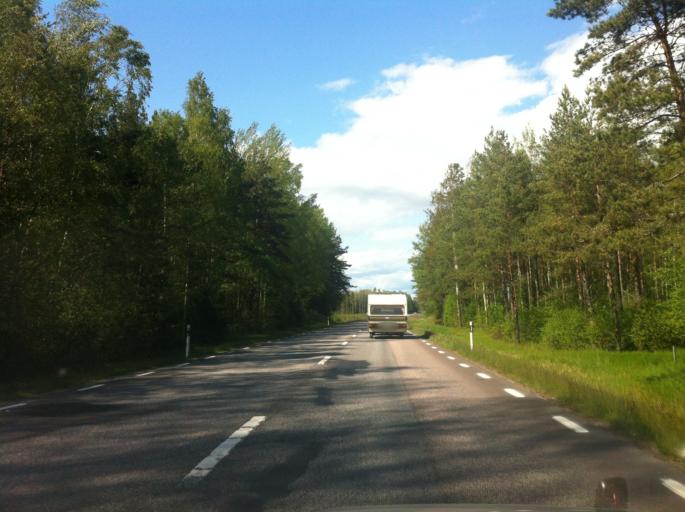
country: SE
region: Vaermland
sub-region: Kristinehamns Kommun
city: Bjorneborg
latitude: 59.1456
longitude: 14.1754
